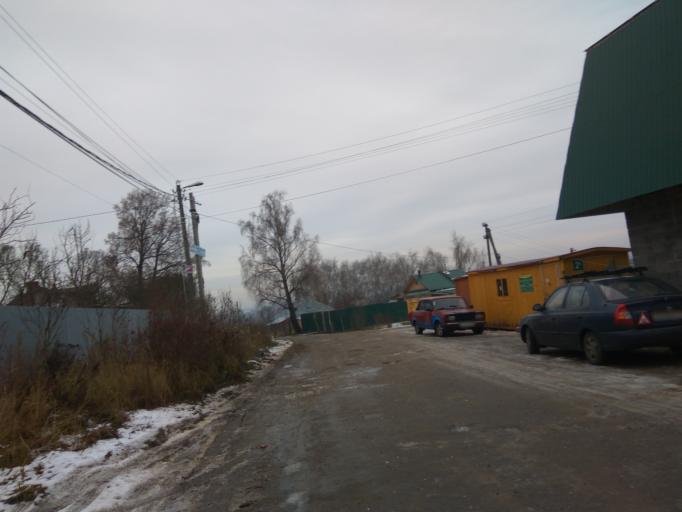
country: RU
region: Moskovskaya
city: Gorki-Leninskiye
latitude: 55.4835
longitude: 37.7919
